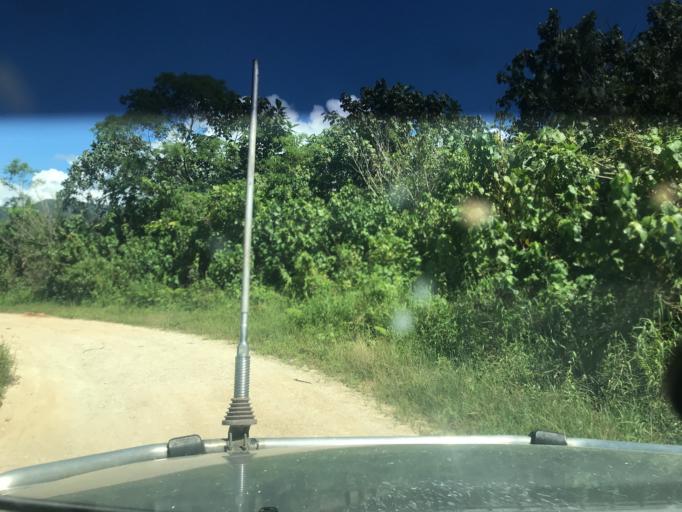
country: SB
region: Malaita
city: Auki
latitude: -8.7298
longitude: 160.9008
